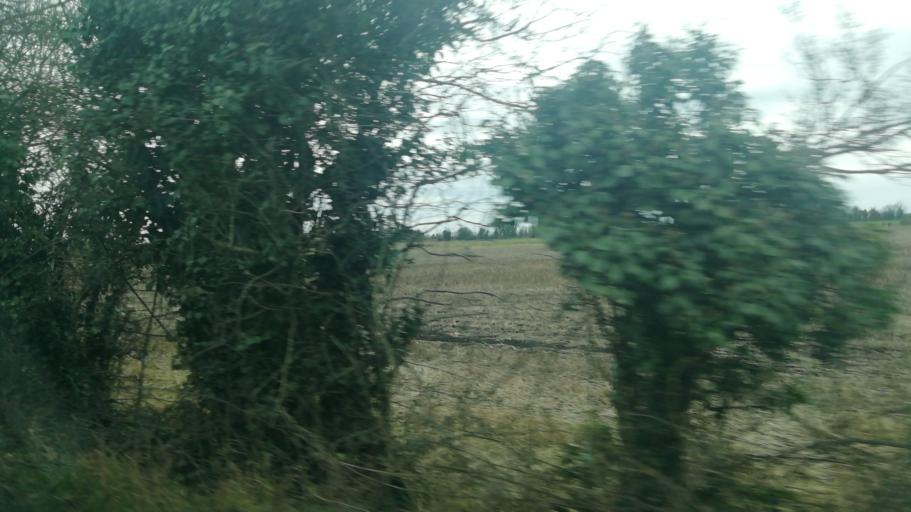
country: IE
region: Leinster
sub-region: Kildare
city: Derrinturn
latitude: 53.2926
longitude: -6.9002
